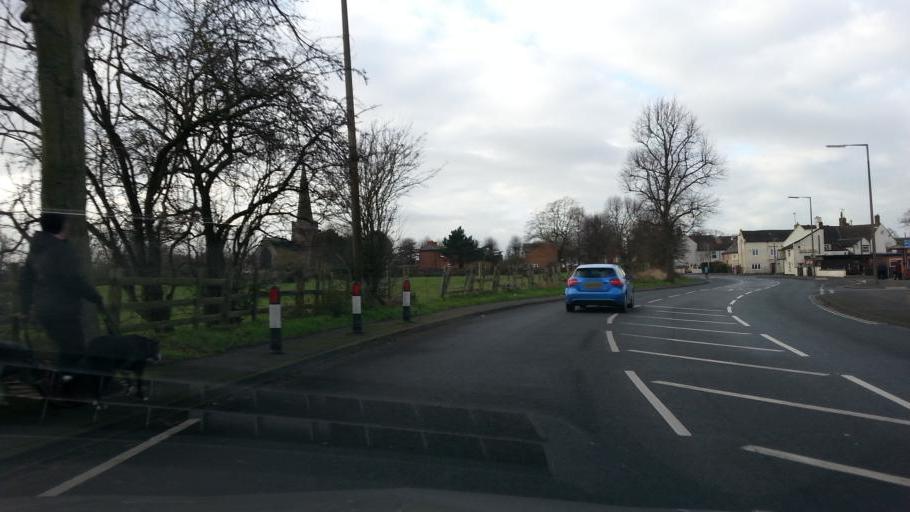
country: GB
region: England
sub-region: Derbyshire
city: Long Eaton
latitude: 52.8787
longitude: -1.2964
